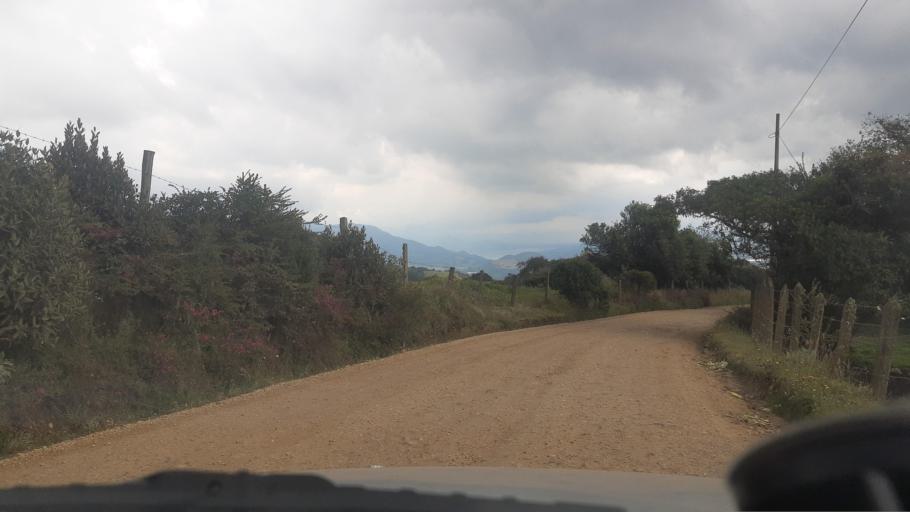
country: CO
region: Cundinamarca
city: Suesca
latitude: 5.1336
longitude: -73.7824
